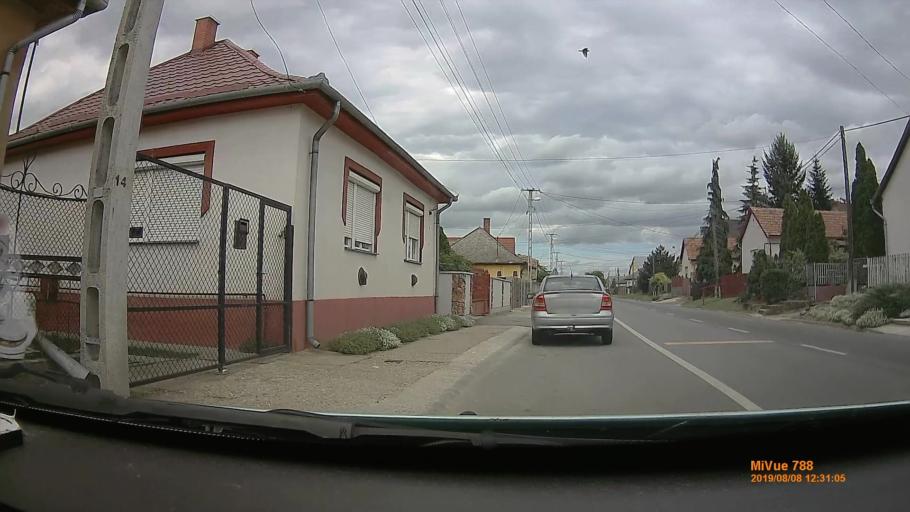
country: HU
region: Szabolcs-Szatmar-Bereg
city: Nyirbator
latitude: 47.8426
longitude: 22.1212
